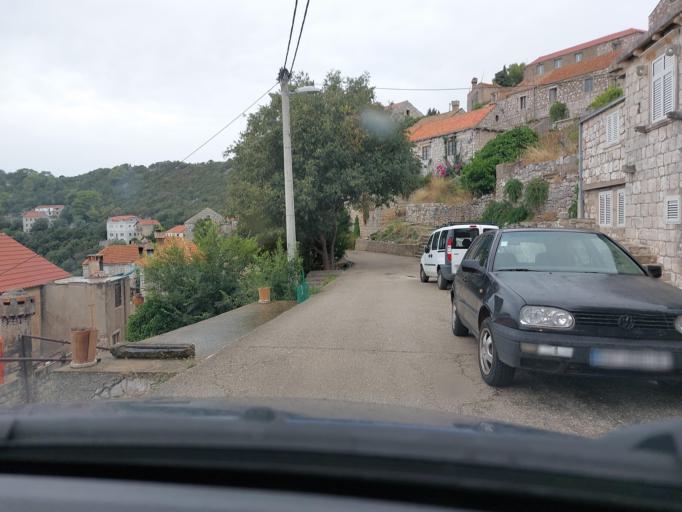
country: HR
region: Dubrovacko-Neretvanska
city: Smokvica
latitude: 42.7679
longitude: 16.8978
